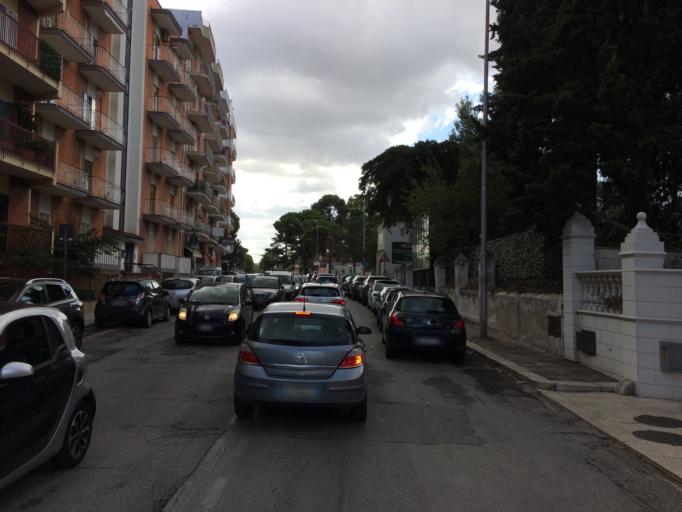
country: IT
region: Apulia
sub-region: Provincia di Bari
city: Bari
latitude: 41.1004
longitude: 16.8799
